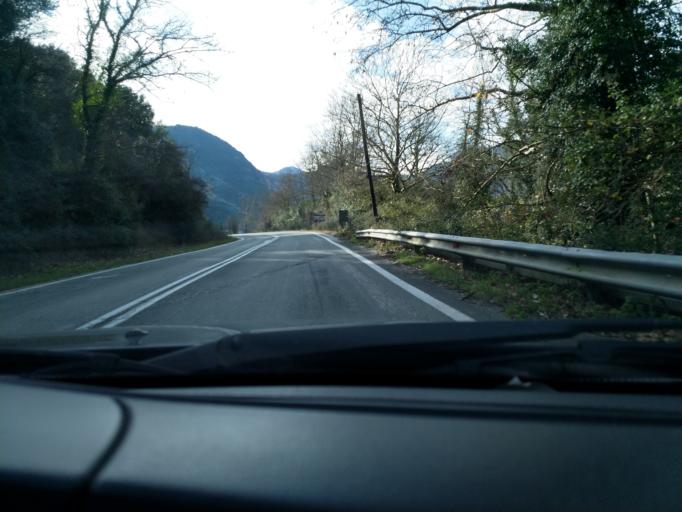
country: GR
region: Epirus
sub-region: Nomos Ioanninon
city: Agia Kyriaki
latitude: 39.4177
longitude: 20.8448
